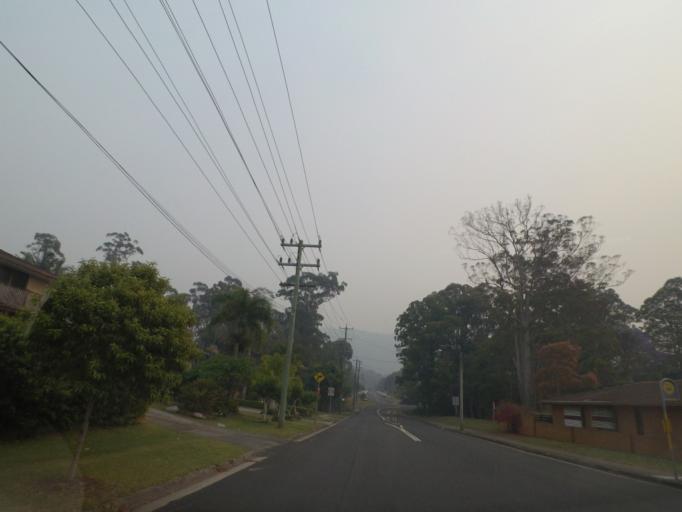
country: AU
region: New South Wales
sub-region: Coffs Harbour
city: Coffs Harbour
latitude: -30.2807
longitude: 153.1036
